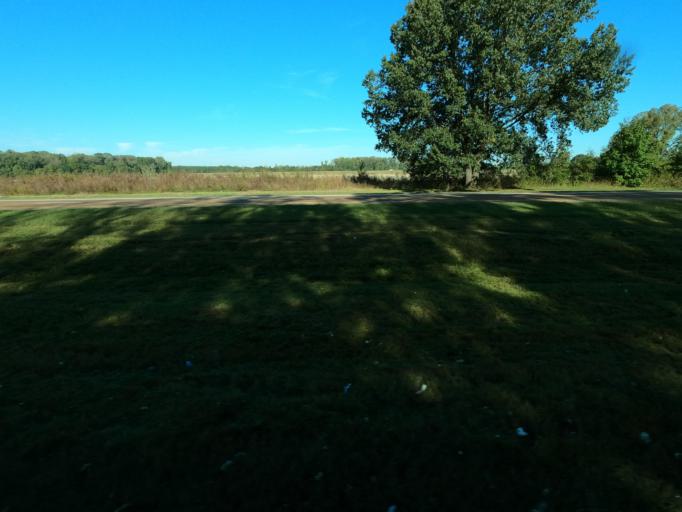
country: US
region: Tennessee
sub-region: Shelby County
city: Millington
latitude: 35.3709
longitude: -89.8816
